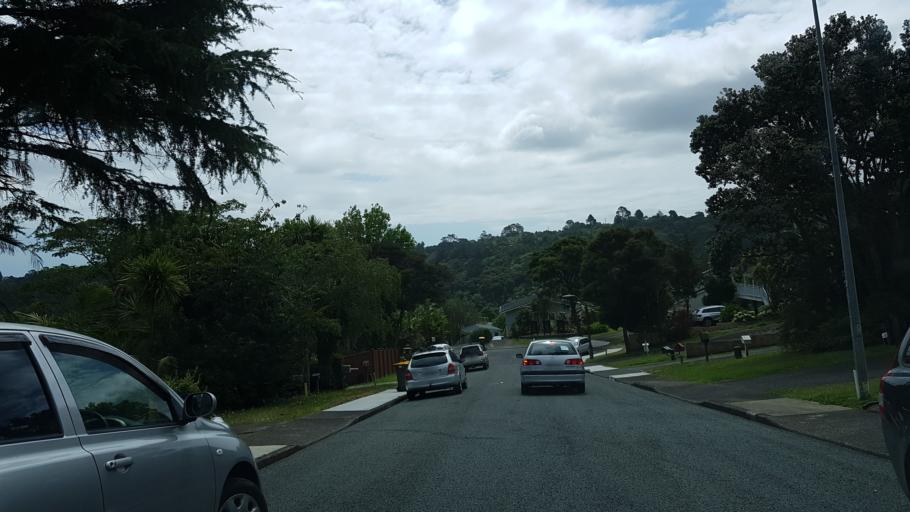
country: NZ
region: Auckland
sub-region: Auckland
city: North Shore
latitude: -36.7751
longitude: 174.7076
